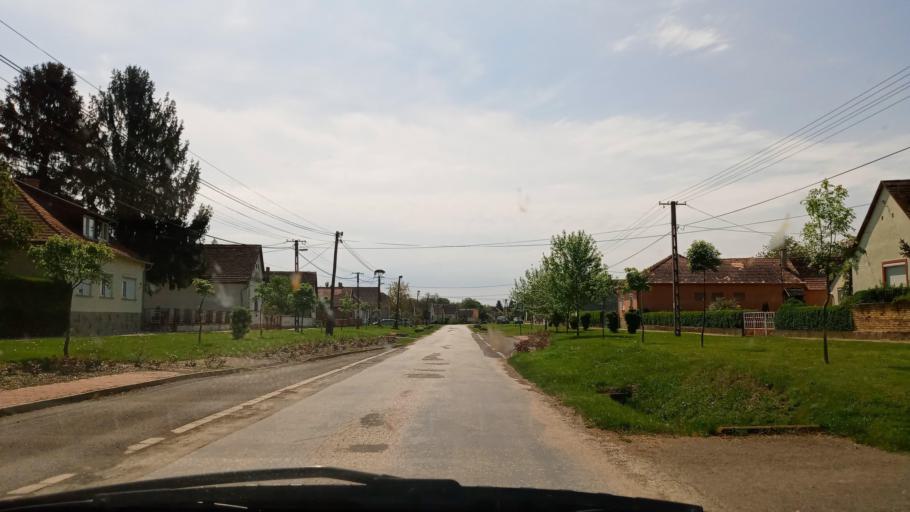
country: HR
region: Osjecko-Baranjska
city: Beli Manastir
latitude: 45.8687
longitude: 18.5847
